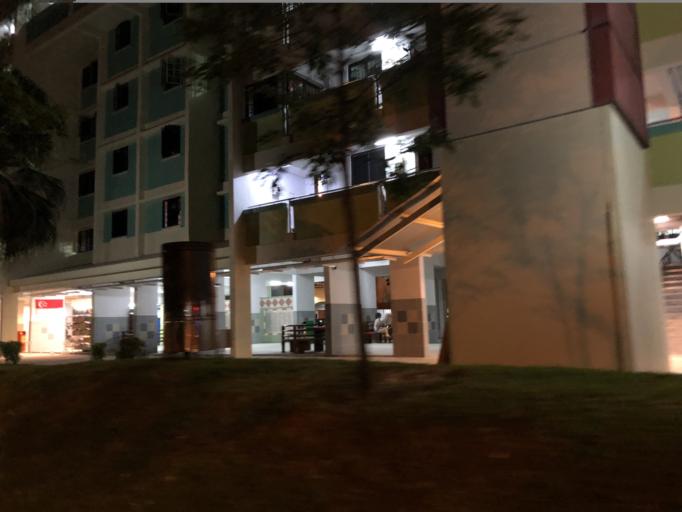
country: MY
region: Johor
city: Kampung Pasir Gudang Baru
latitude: 1.4317
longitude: 103.8379
